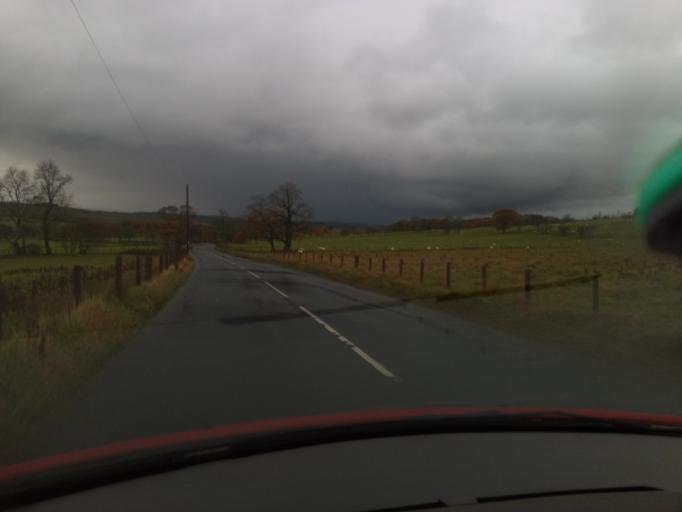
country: GB
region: England
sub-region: Northumberland
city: Birtley
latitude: 55.1199
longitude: -2.2341
